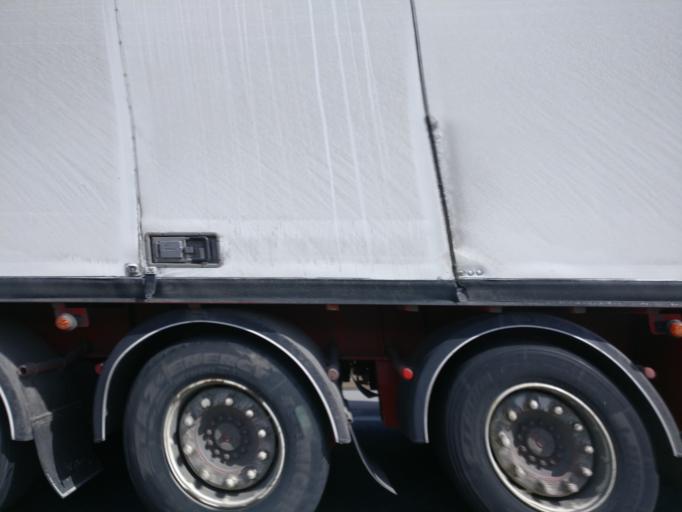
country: FI
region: Haeme
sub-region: Riihimaeki
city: Riihimaeki
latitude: 60.7797
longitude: 24.7093
